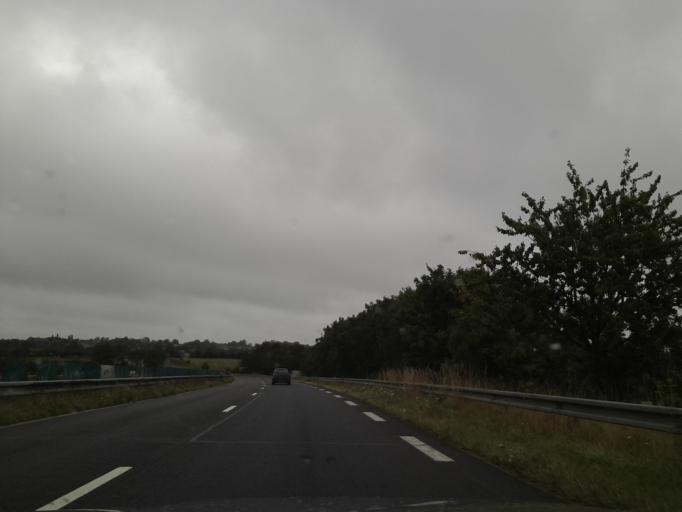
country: FR
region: Lower Normandy
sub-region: Departement de la Manche
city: Sainte-Mere-Eglise
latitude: 49.3626
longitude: -1.2800
